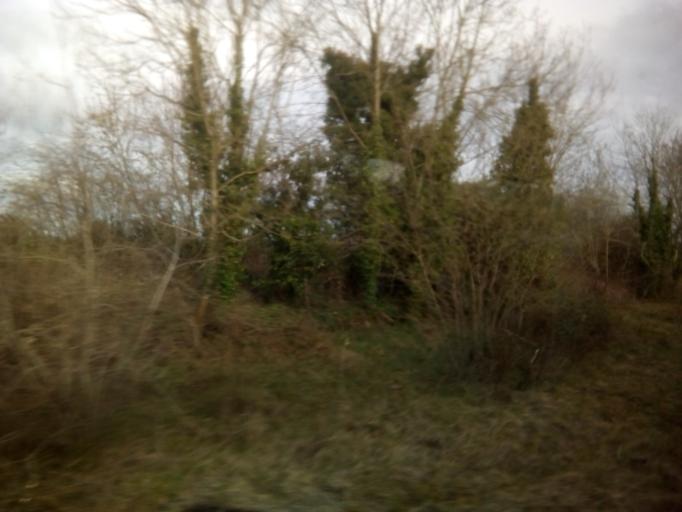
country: IE
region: Leinster
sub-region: Kildare
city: Kilcock
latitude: 53.4073
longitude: -6.6829
